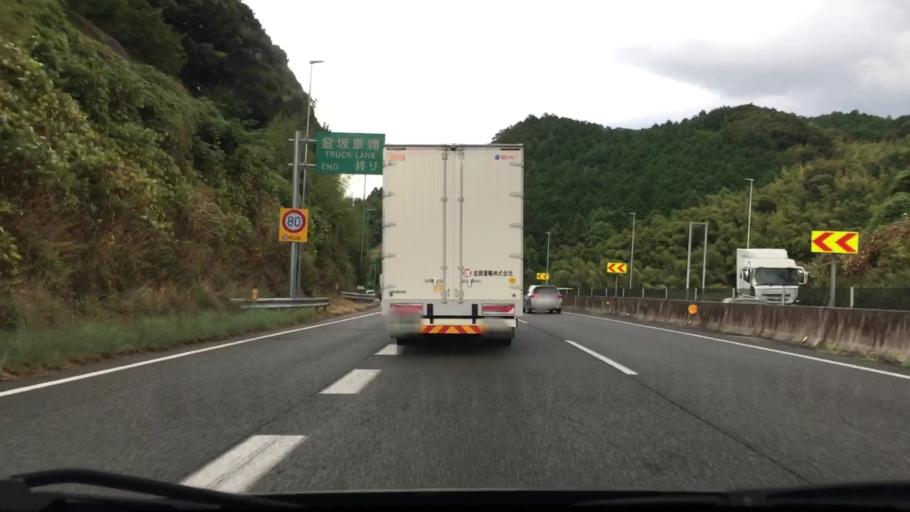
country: JP
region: Fukuoka
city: Nishifukuma
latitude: 33.7491
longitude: 130.5574
